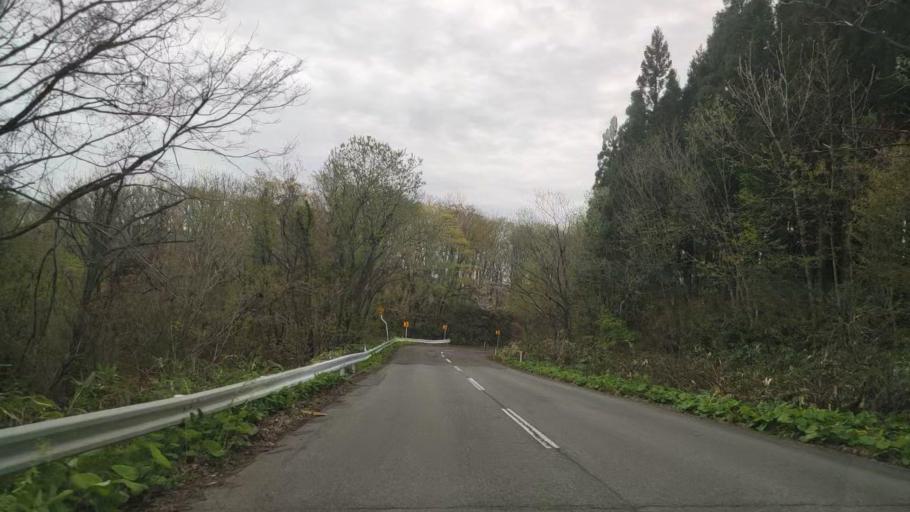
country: JP
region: Akita
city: Hanawa
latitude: 40.3756
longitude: 140.7896
